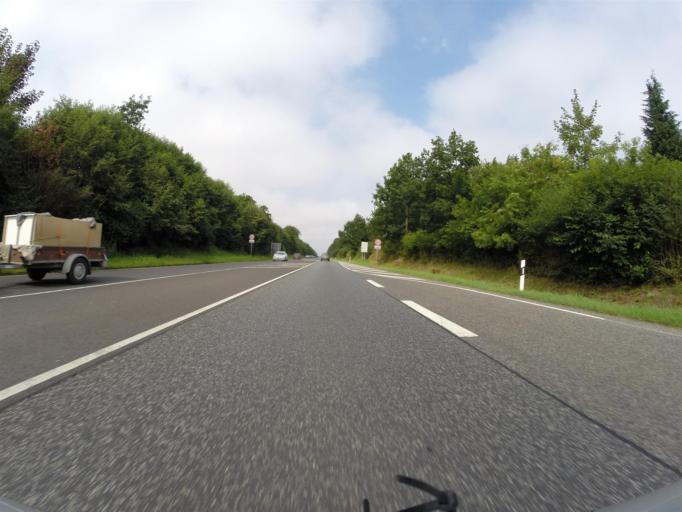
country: DE
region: Hesse
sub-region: Regierungsbezirk Kassel
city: Kaufungen
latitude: 51.2776
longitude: 9.6167
